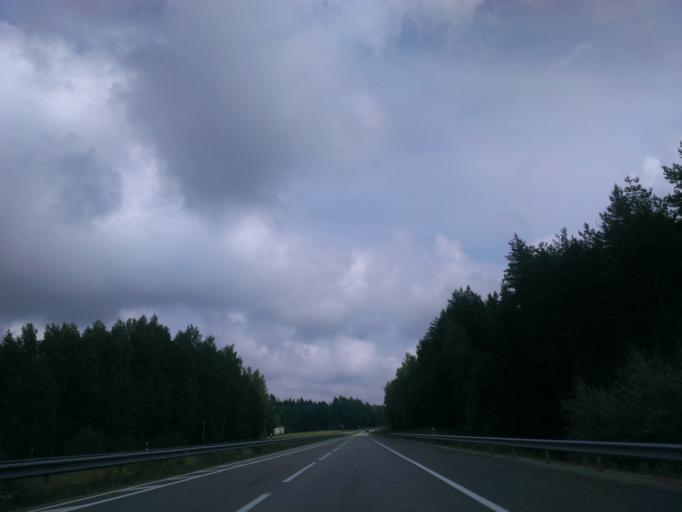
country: LV
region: Krimulda
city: Ragana
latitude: 57.1342
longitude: 24.7718
